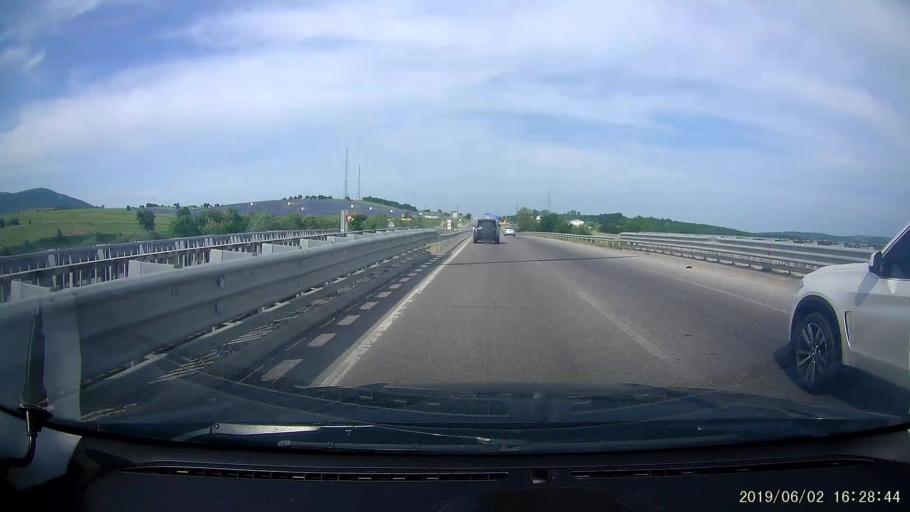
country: TR
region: Samsun
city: Ladik
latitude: 41.0082
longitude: 35.8549
